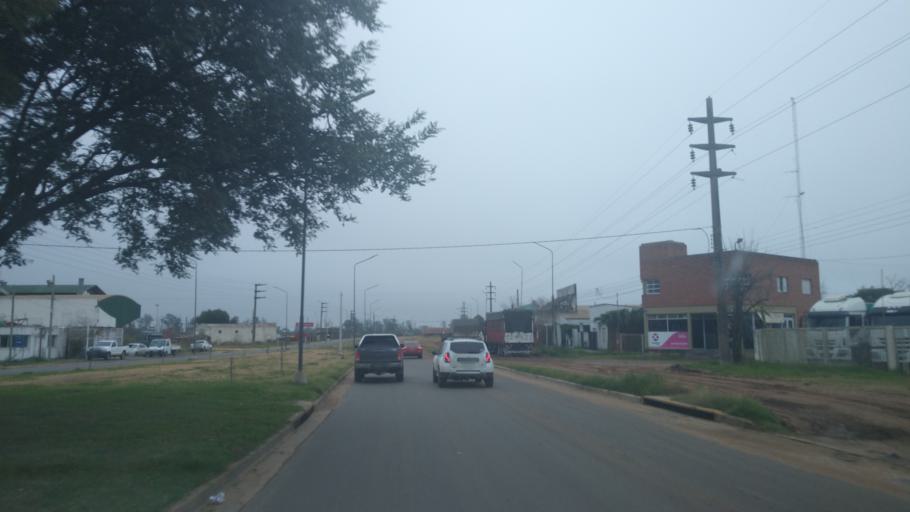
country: AR
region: Entre Rios
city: Chajari
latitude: -30.7619
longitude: -58.0115
